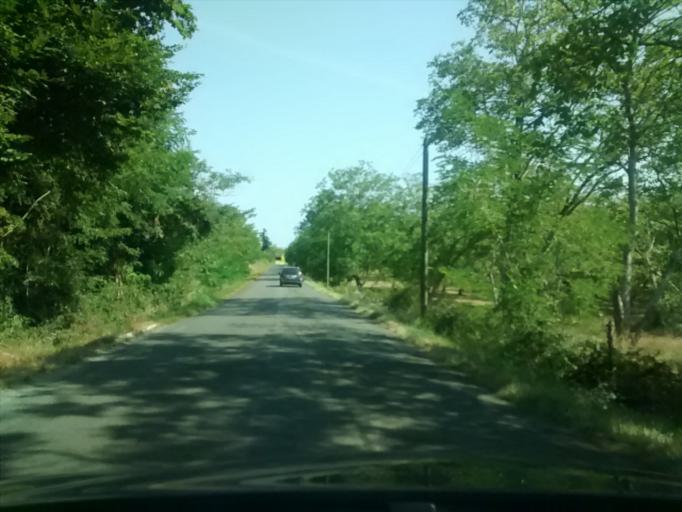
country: FR
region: Aquitaine
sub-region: Departement de la Dordogne
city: Lalinde
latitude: 44.8640
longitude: 0.7519
